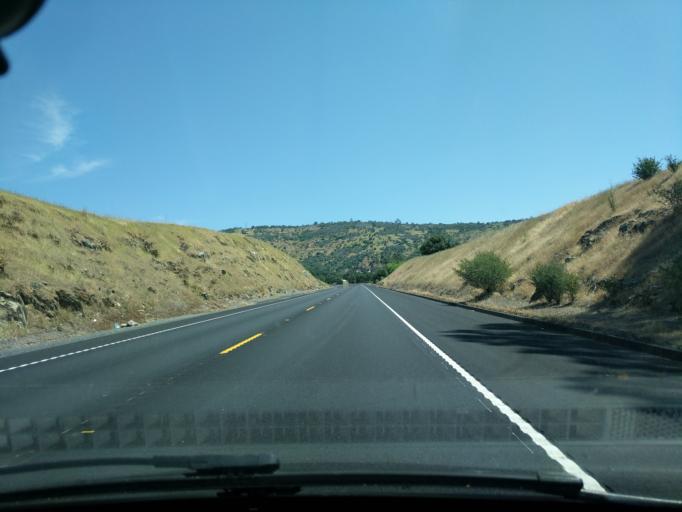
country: US
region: California
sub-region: Calaveras County
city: Copperopolis
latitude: 37.9738
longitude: -120.6545
